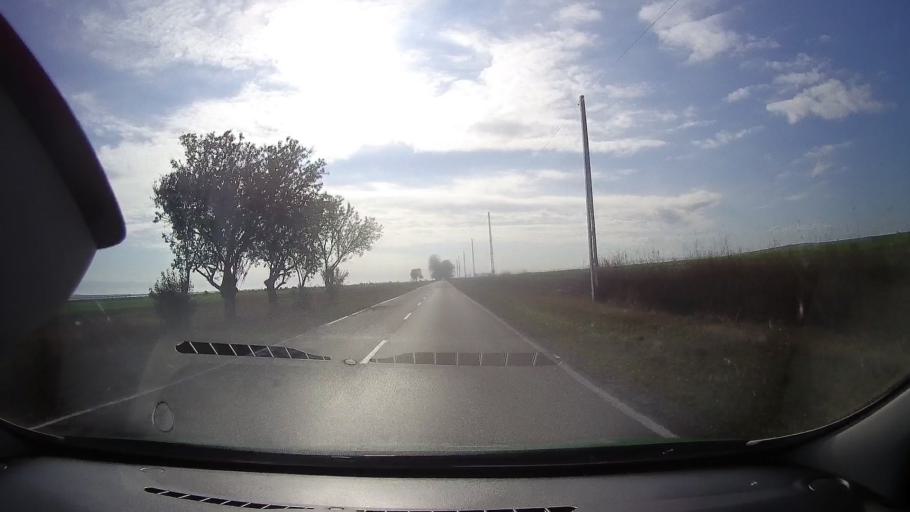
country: RO
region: Tulcea
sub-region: Comuna Valea Nucarilor
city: Agighiol
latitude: 45.0167
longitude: 28.8833
